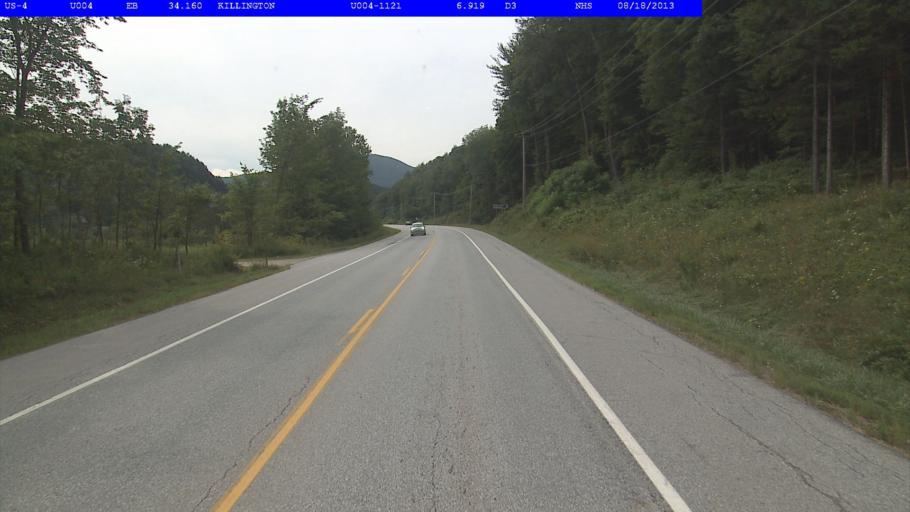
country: US
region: Vermont
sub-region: Rutland County
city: Rutland
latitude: 43.6212
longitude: -72.7599
